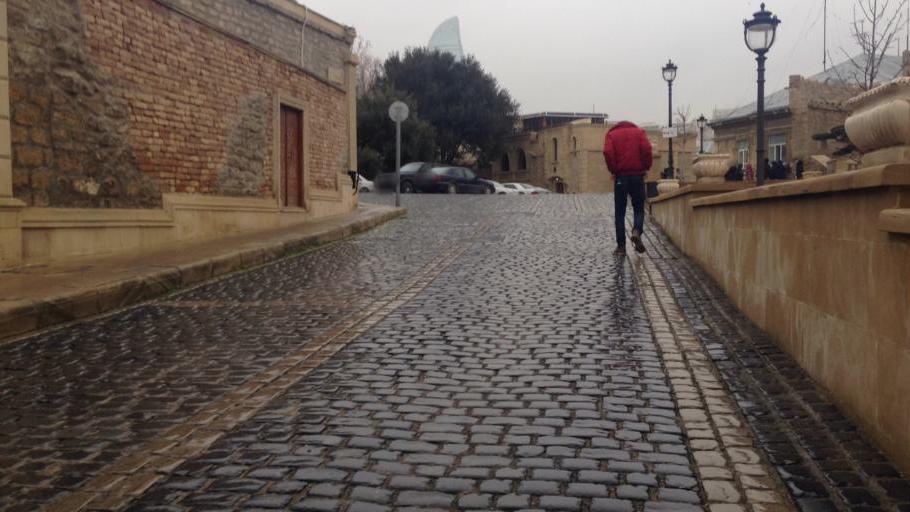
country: AZ
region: Baki
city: Badamdar
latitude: 40.3674
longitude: 49.8332
